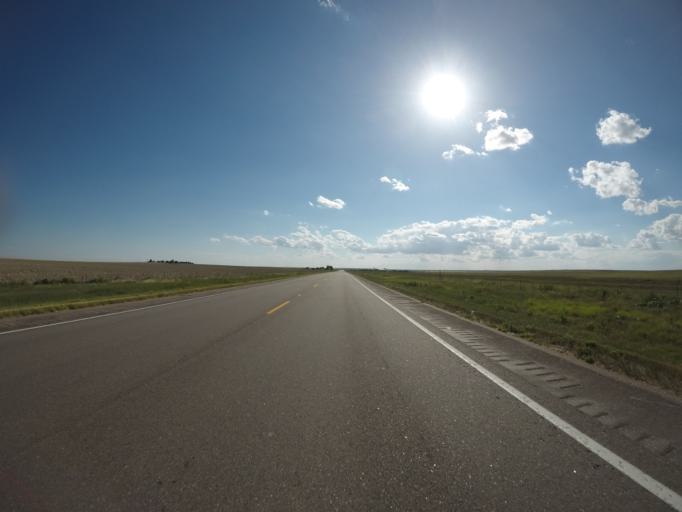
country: US
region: Colorado
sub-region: Morgan County
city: Fort Morgan
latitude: 40.6011
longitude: -103.8639
